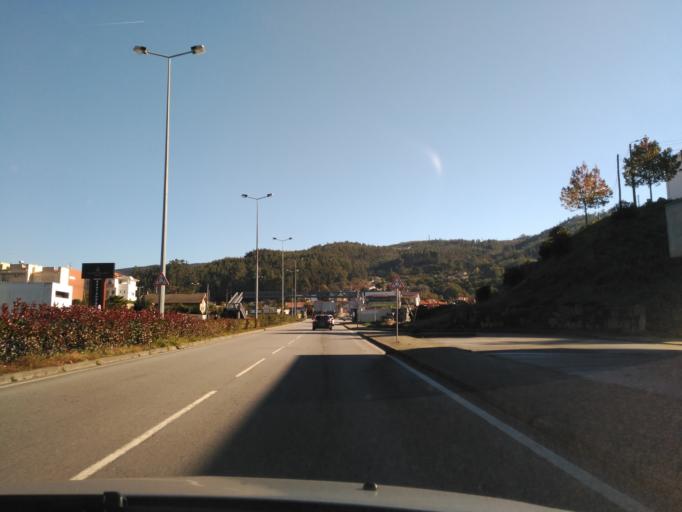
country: PT
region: Braga
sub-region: Braga
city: Adaufe
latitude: 41.5665
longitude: -8.3739
